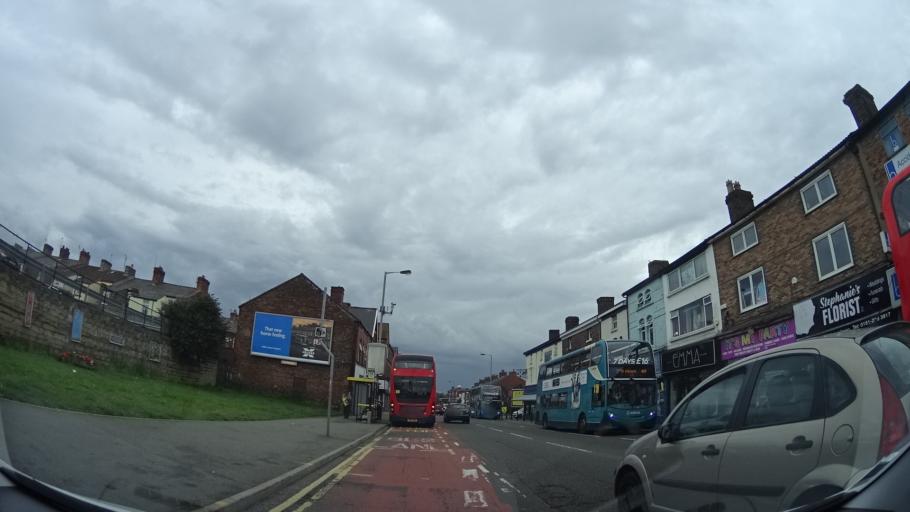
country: GB
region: England
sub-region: Liverpool
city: Liverpool
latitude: 53.4140
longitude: -2.9151
